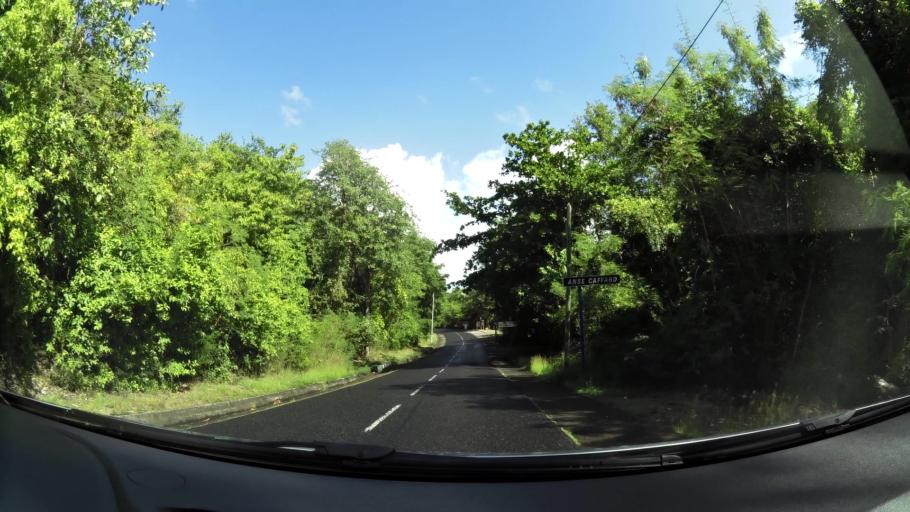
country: MQ
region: Martinique
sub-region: Martinique
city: Les Trois-Ilets
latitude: 14.4611
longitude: -61.0478
